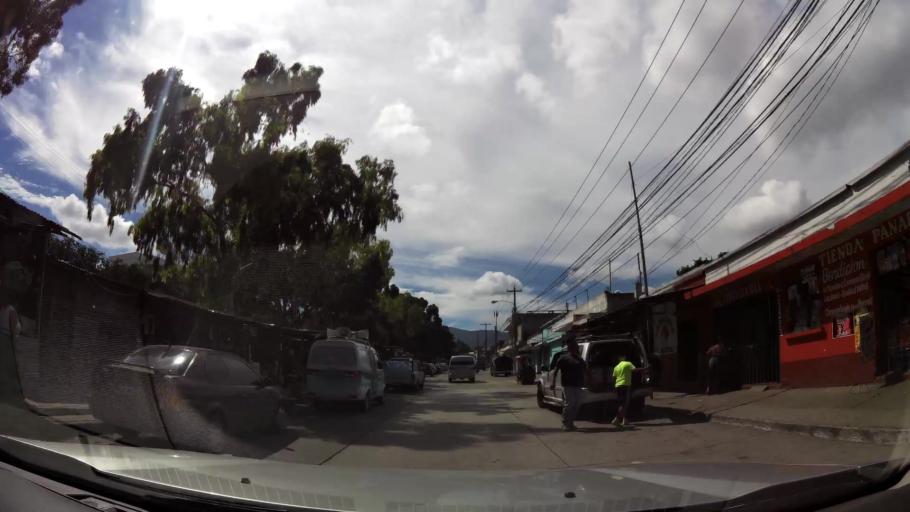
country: GT
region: Guatemala
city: Mixco
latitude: 14.6492
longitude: -90.5805
